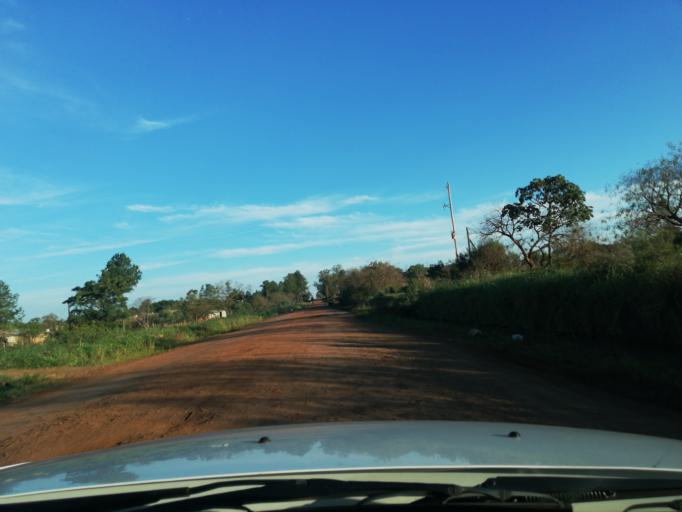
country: AR
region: Misiones
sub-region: Departamento de Capital
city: Posadas
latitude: -27.4727
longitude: -55.9708
